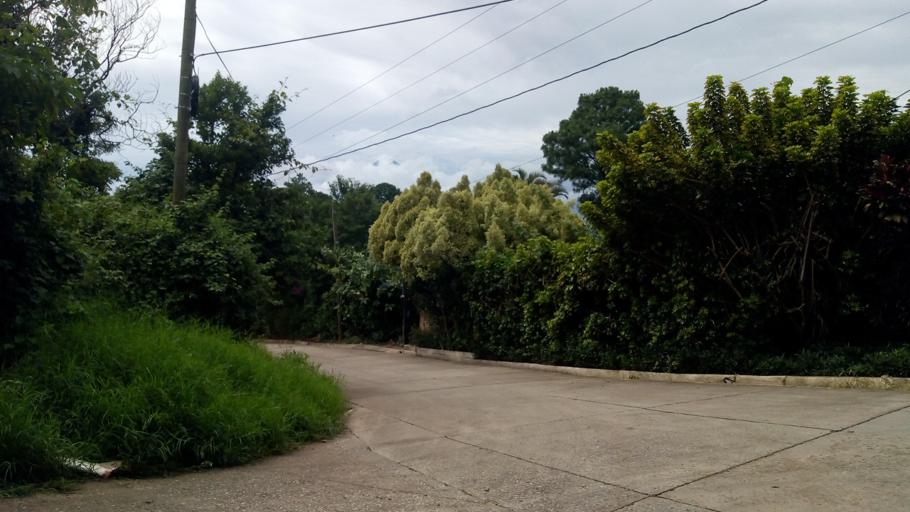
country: GT
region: Guatemala
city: Villa Canales
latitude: 14.5091
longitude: -90.5171
